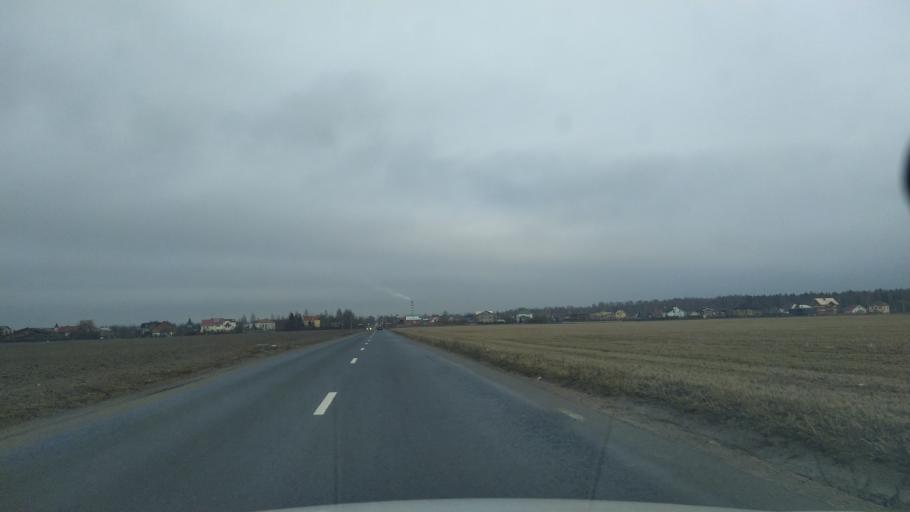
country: RU
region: St.-Petersburg
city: Aleksandrovskaya
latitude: 59.7189
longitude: 30.3412
